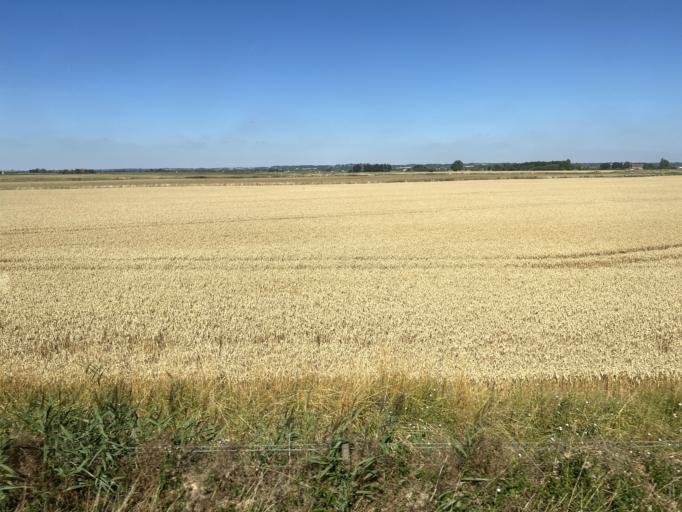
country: GB
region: England
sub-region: Lincolnshire
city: Spilsby
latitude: 53.1170
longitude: 0.1321
